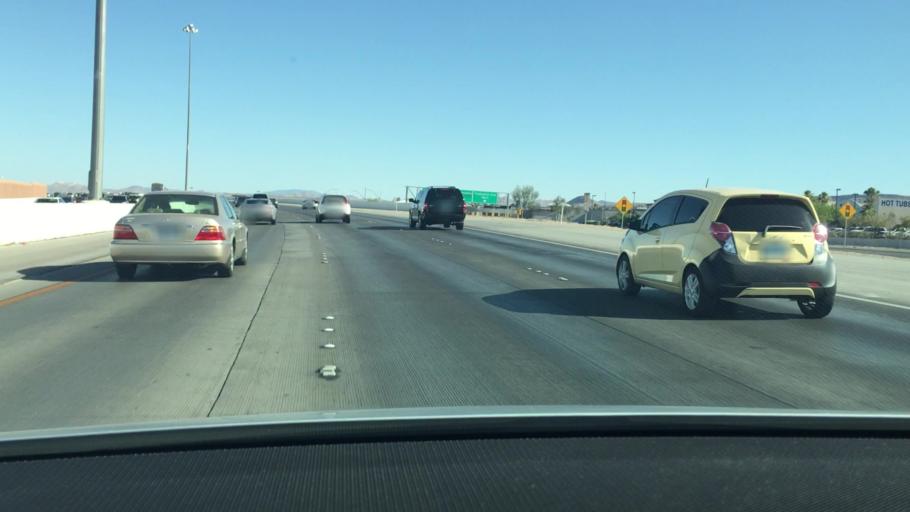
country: US
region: Nevada
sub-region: Clark County
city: Summerlin South
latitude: 36.1025
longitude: -115.2952
